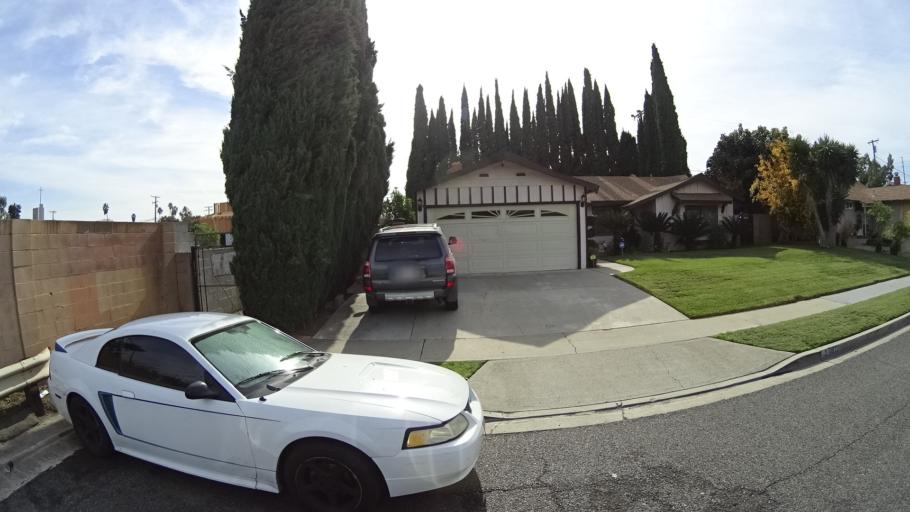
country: US
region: California
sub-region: Orange County
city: Garden Grove
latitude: 33.7898
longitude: -117.9049
